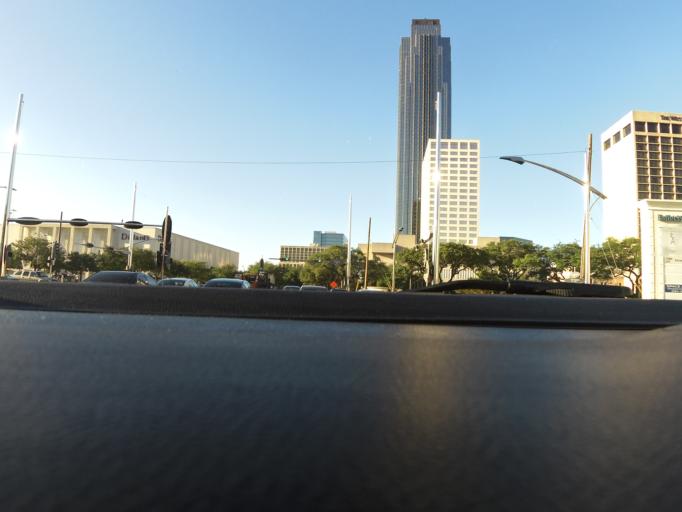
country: US
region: Texas
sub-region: Harris County
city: Bellaire
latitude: 29.7414
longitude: -95.4611
